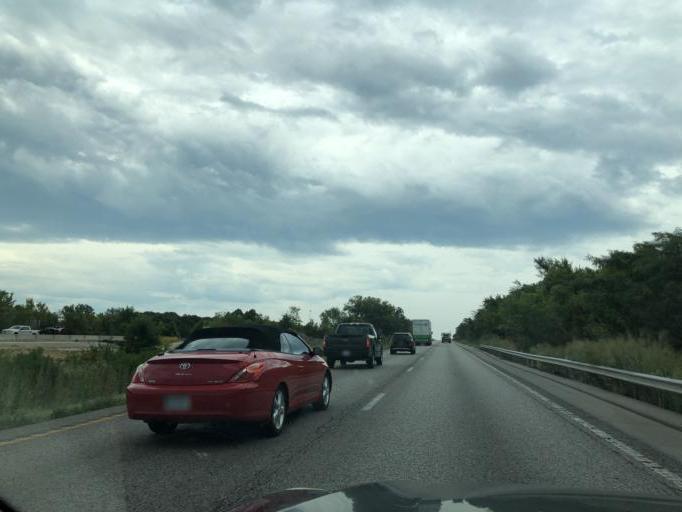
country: US
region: Missouri
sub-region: Montgomery County
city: Montgomery City
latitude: 38.9007
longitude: -91.5779
